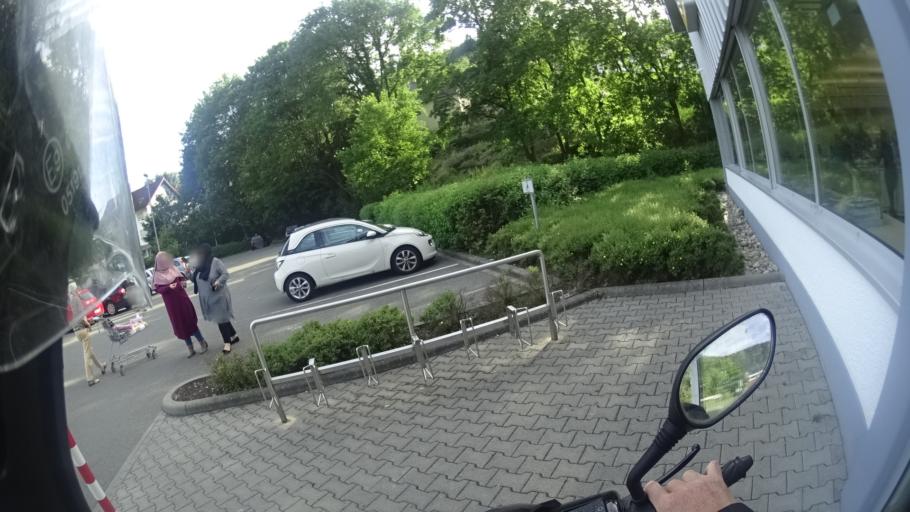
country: DE
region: Hesse
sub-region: Regierungsbezirk Darmstadt
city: Bad Schwalbach
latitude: 50.1504
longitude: 8.0815
